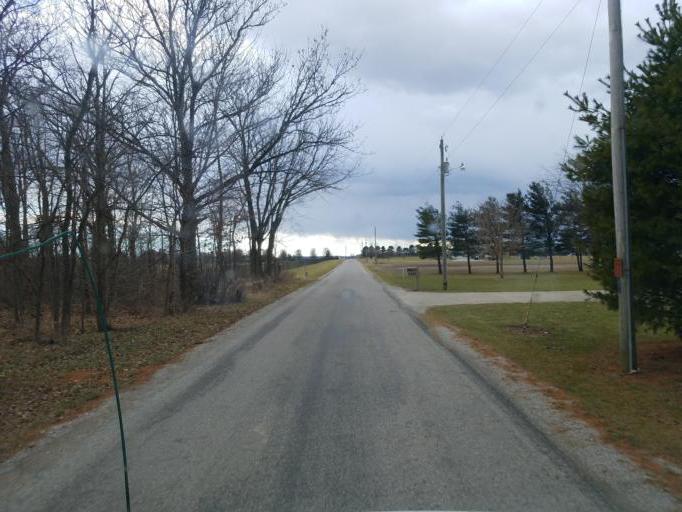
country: US
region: Ohio
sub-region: Marion County
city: Prospect
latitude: 40.4588
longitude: -83.1120
